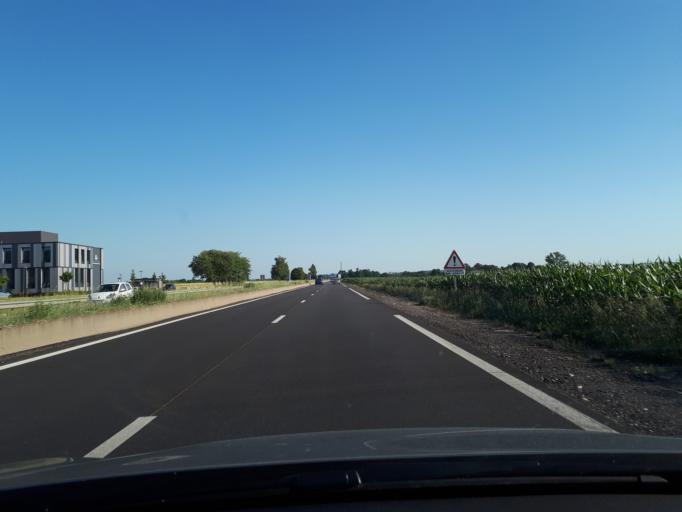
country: FR
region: Rhone-Alpes
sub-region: Departement du Rhone
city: Saint-Laurent-de-Mure
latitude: 45.7122
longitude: 5.0708
